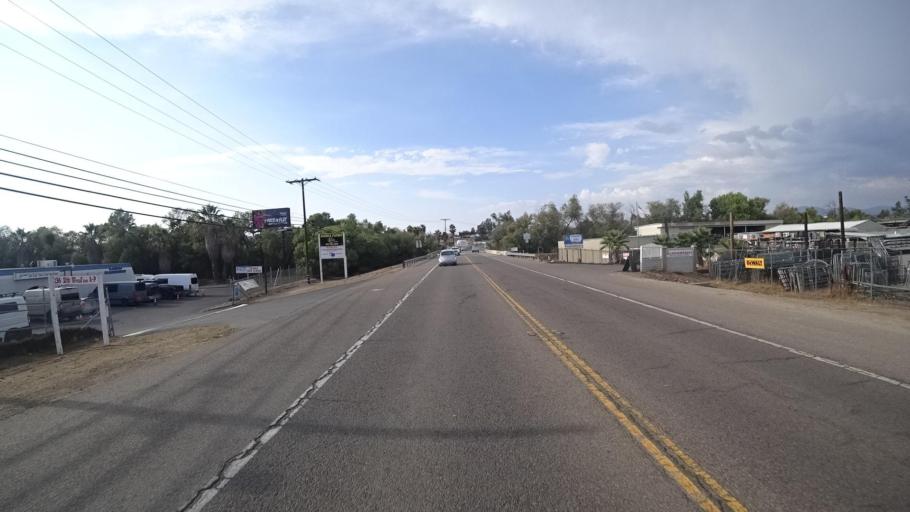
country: US
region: California
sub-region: San Diego County
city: Ramona
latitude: 33.0444
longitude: -116.8703
